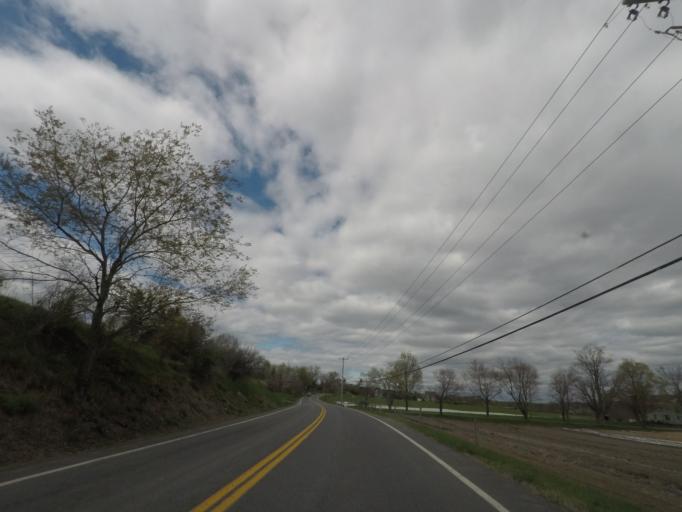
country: US
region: New York
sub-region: Columbia County
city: Philmont
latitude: 42.2709
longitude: -73.6615
